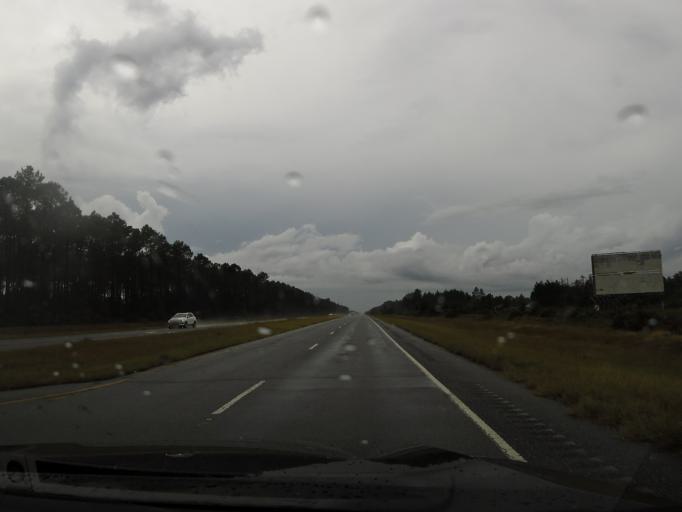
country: US
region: Georgia
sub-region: Wayne County
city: Jesup
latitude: 31.4763
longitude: -81.7273
